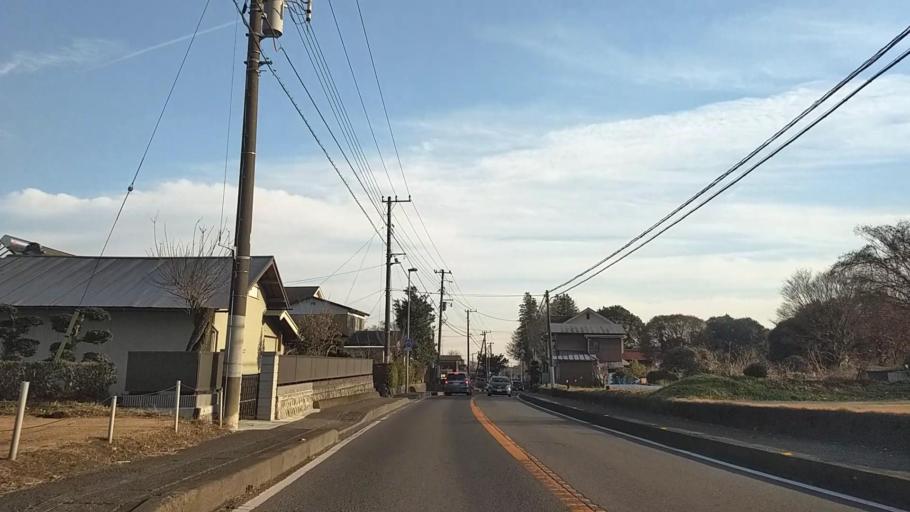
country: JP
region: Kanagawa
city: Zama
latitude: 35.5124
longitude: 139.3013
